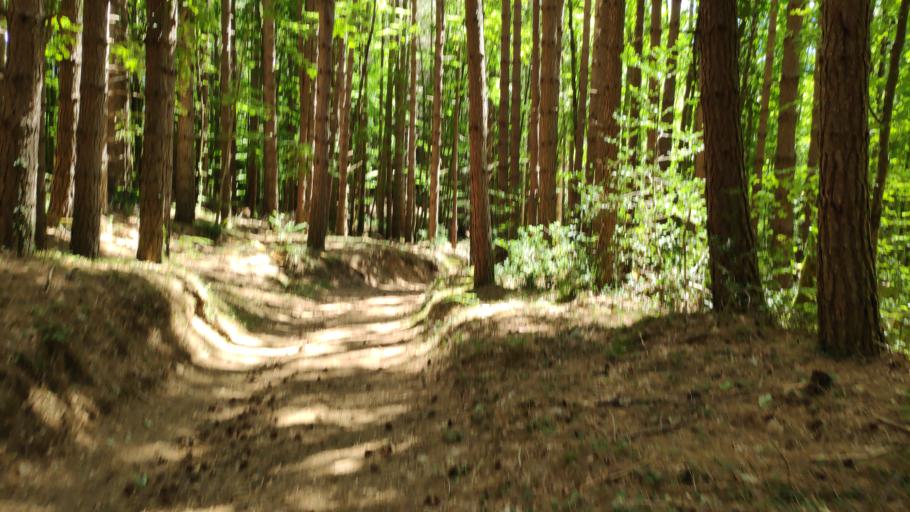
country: IT
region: Calabria
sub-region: Provincia di Vibo-Valentia
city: Nardodipace
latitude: 38.5056
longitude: 16.3730
